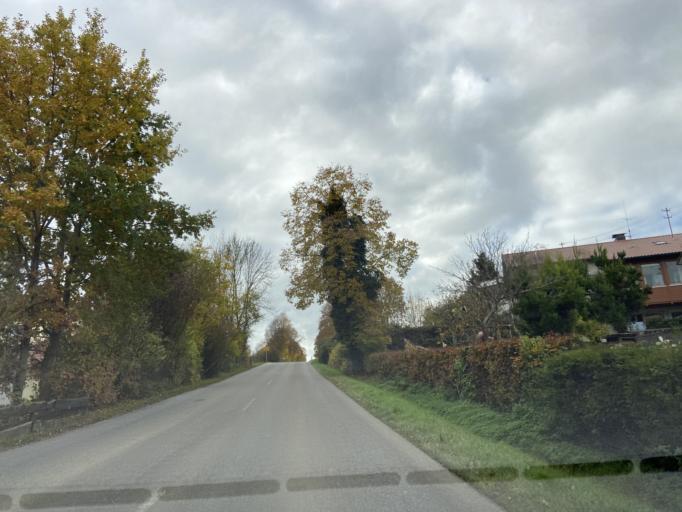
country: DE
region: Baden-Wuerttemberg
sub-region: Tuebingen Region
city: Inzigkofen
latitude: 48.0722
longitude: 9.1879
